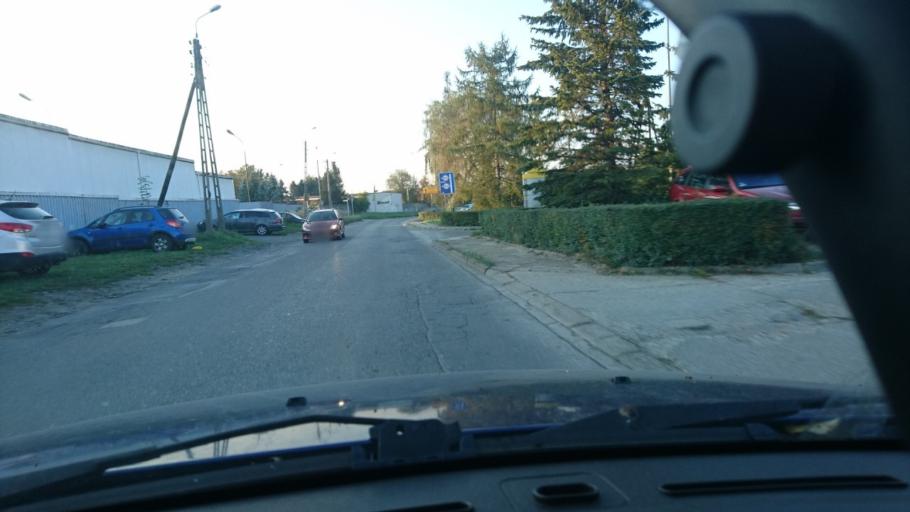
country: PL
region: Silesian Voivodeship
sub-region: Powiat bielski
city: Jaworze
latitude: 49.8132
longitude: 18.9834
